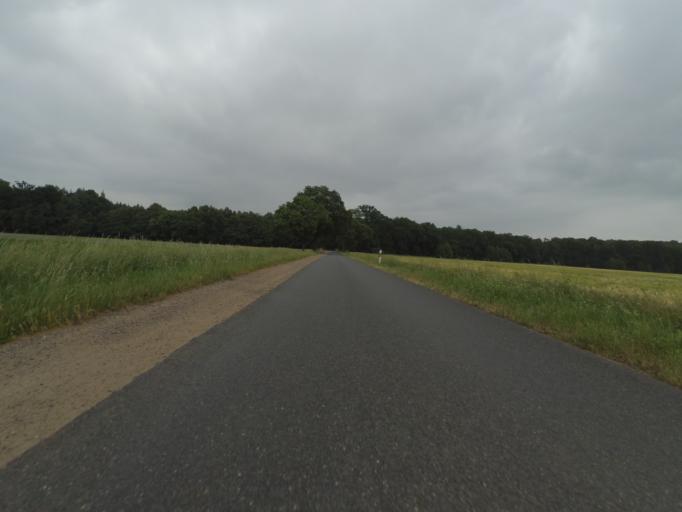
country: DE
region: Mecklenburg-Vorpommern
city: Spornitz
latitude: 53.3623
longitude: 11.6959
